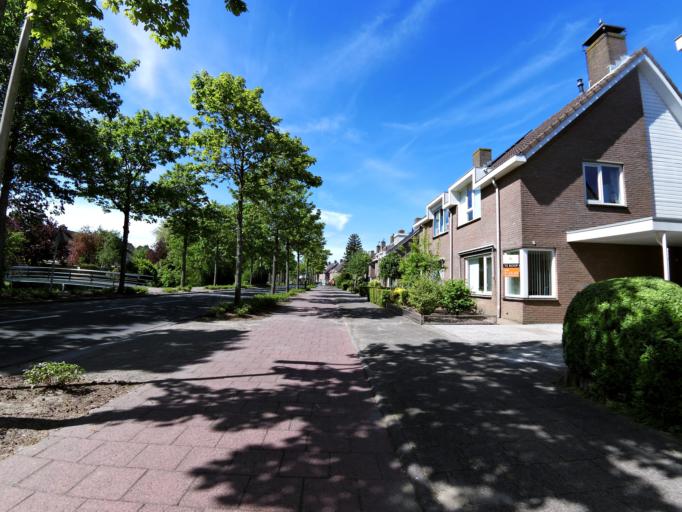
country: NL
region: South Holland
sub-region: Gemeente Hellevoetsluis
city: Nieuwenhoorn
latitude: 51.8404
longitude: 4.1550
